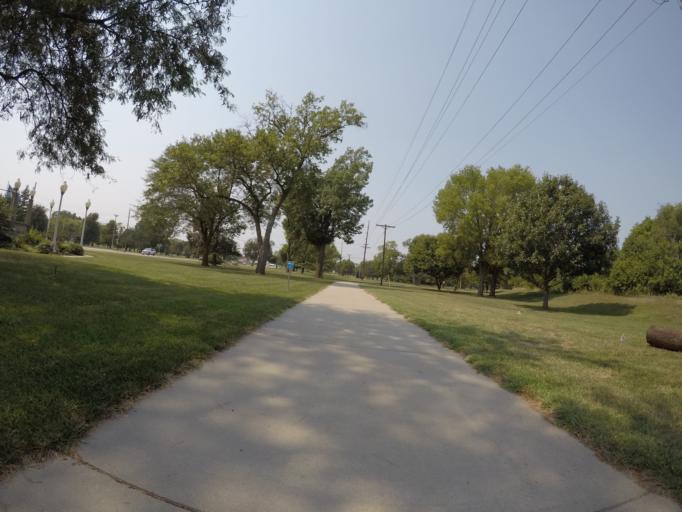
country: US
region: Nebraska
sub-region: Gage County
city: Beatrice
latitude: 40.2663
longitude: -96.7574
